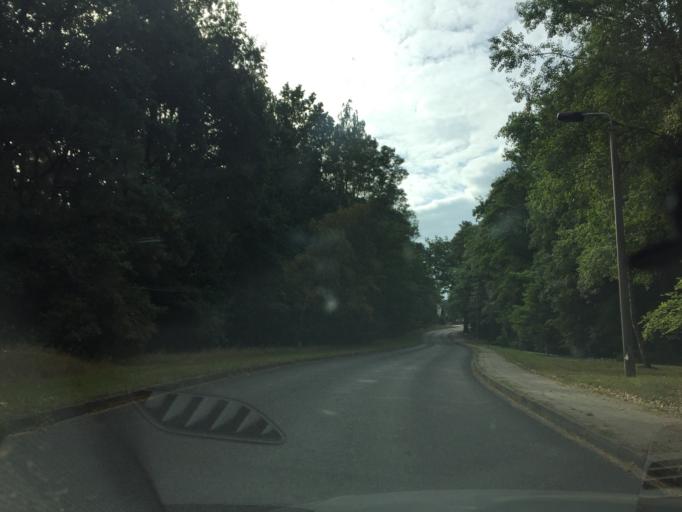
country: DE
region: Brandenburg
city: Erkner
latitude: 52.4129
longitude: 13.7634
